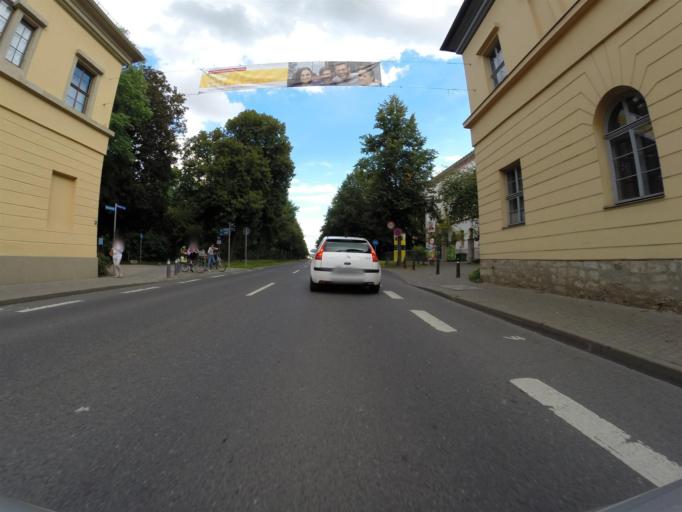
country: DE
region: Thuringia
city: Weimar
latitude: 50.9748
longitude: 11.3298
